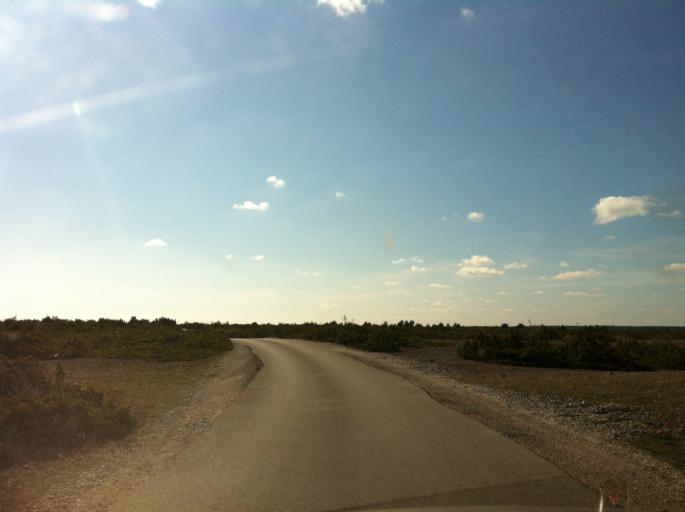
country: SE
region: Gotland
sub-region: Gotland
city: Slite
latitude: 57.9928
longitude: 19.1675
